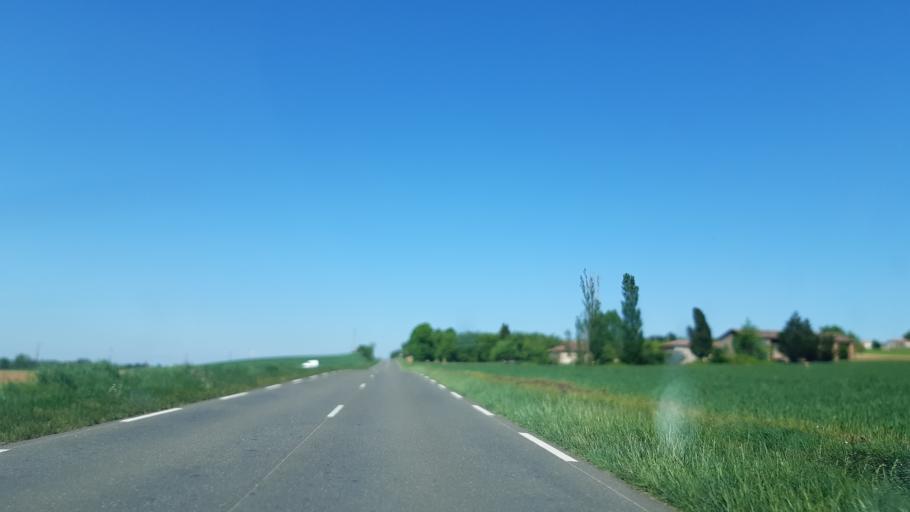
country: FR
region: Midi-Pyrenees
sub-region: Departement du Gers
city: Pujaudran
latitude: 43.5770
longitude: 1.0408
